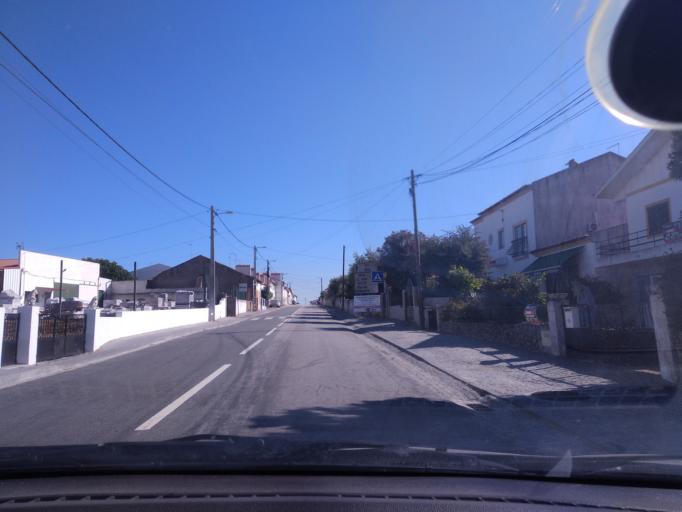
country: PT
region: Portalegre
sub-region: Portalegre
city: Alagoa
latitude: 39.4185
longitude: -7.6204
